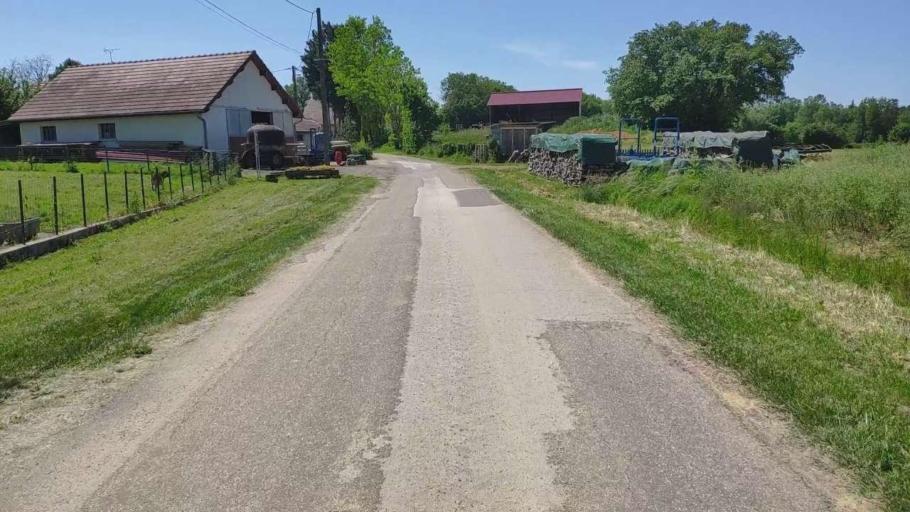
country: FR
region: Franche-Comte
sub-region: Departement du Jura
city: Bletterans
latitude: 46.7455
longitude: 5.4078
